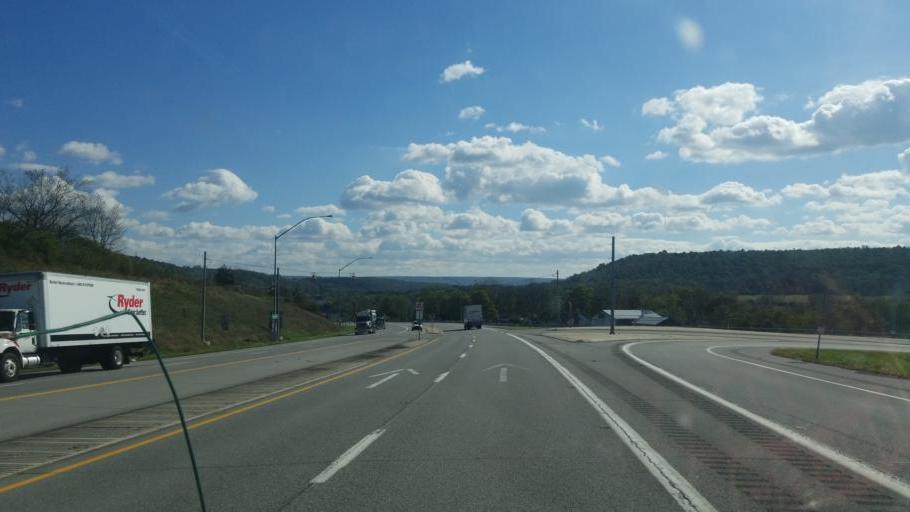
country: US
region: Pennsylvania
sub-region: Bedford County
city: Earlston
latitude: 40.0206
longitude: -78.3521
